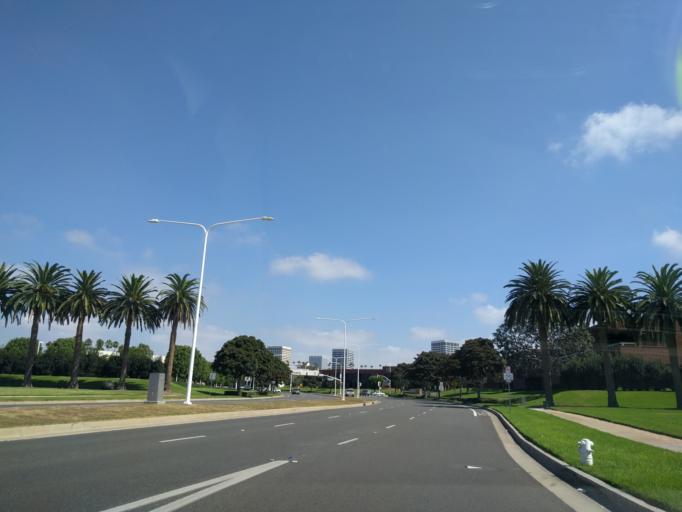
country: US
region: California
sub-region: Orange County
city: San Joaquin Hills
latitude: 33.6080
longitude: -117.8784
